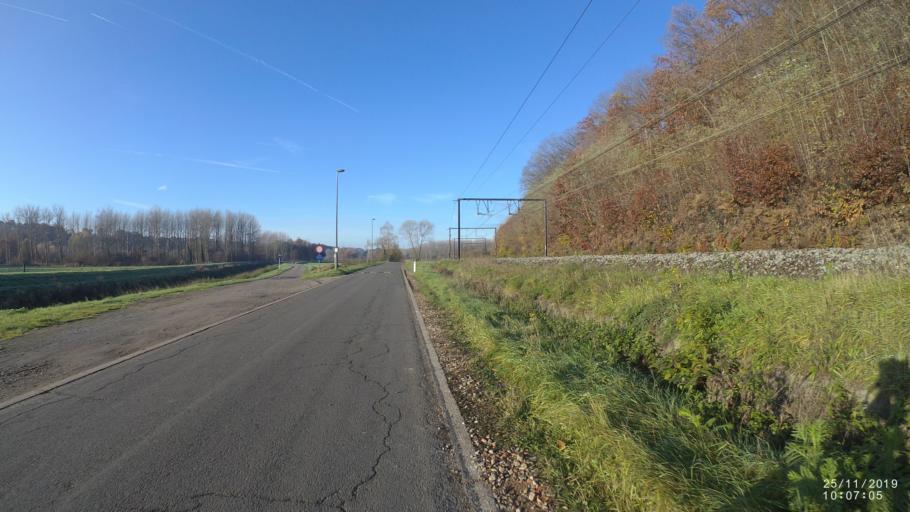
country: BE
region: Flanders
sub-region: Provincie Vlaams-Brabant
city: Diest
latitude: 50.9915
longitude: 5.0242
